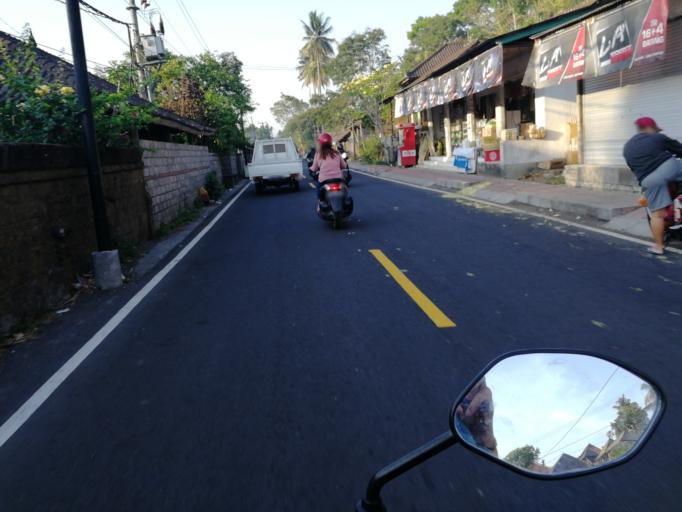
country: ID
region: Bali
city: Tistagede
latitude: -8.3793
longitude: 115.6089
